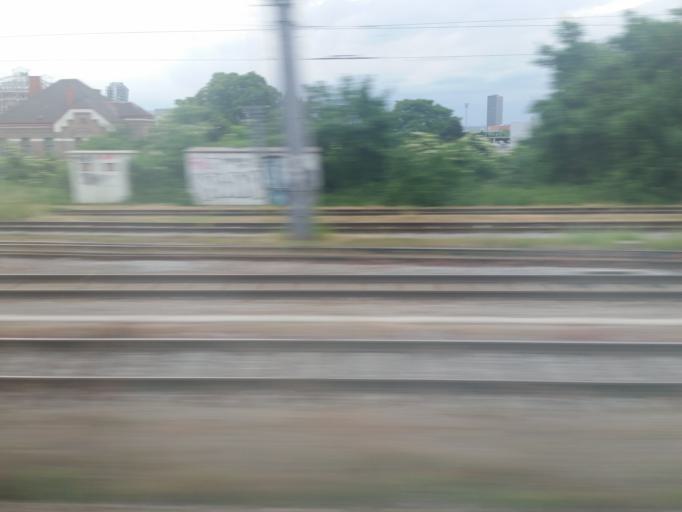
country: AT
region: Vienna
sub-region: Wien Stadt
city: Vienna
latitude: 48.1850
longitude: 16.4303
